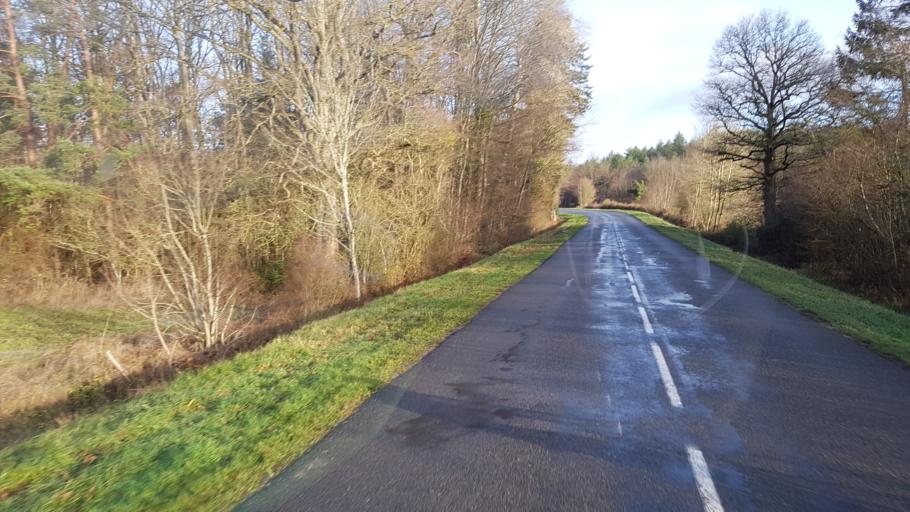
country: FR
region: Centre
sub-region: Departement du Loiret
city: Chilleurs-aux-Bois
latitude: 48.0122
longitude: 2.2010
